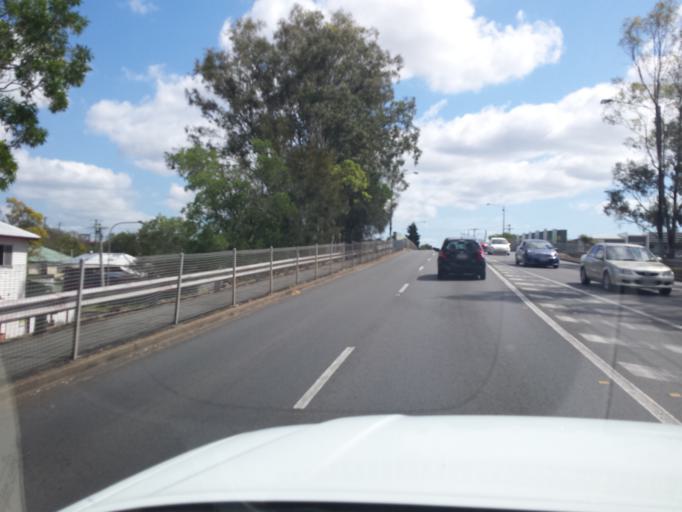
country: AU
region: Queensland
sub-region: Brisbane
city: Zillmere
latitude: -27.3613
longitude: 153.0378
